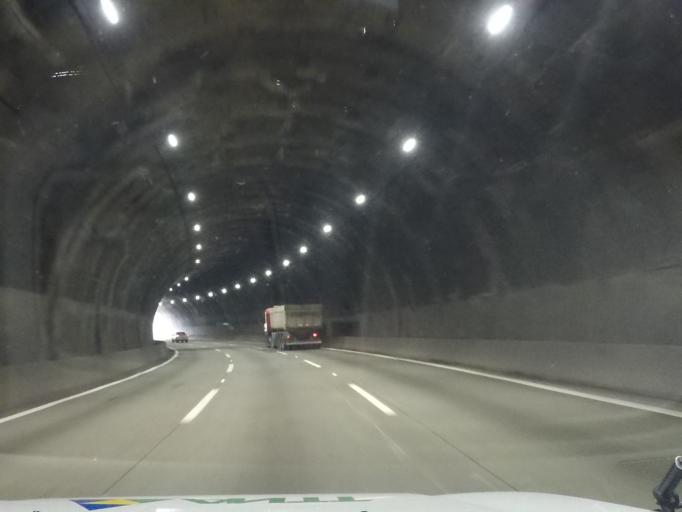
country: BR
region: Sao Paulo
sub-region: Mairipora
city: Mairipora
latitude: -23.3568
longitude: -46.5488
